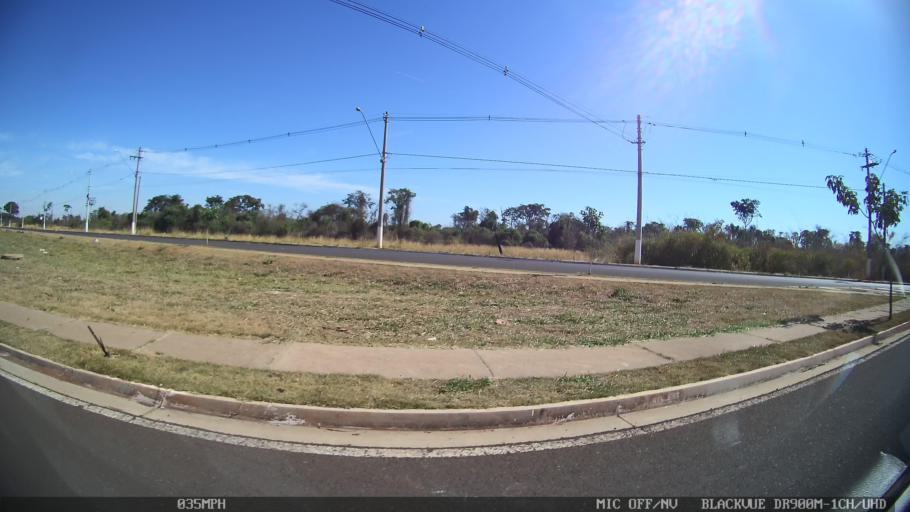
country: BR
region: Sao Paulo
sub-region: Sao Jose Do Rio Preto
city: Sao Jose do Rio Preto
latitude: -20.7461
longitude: -49.4354
